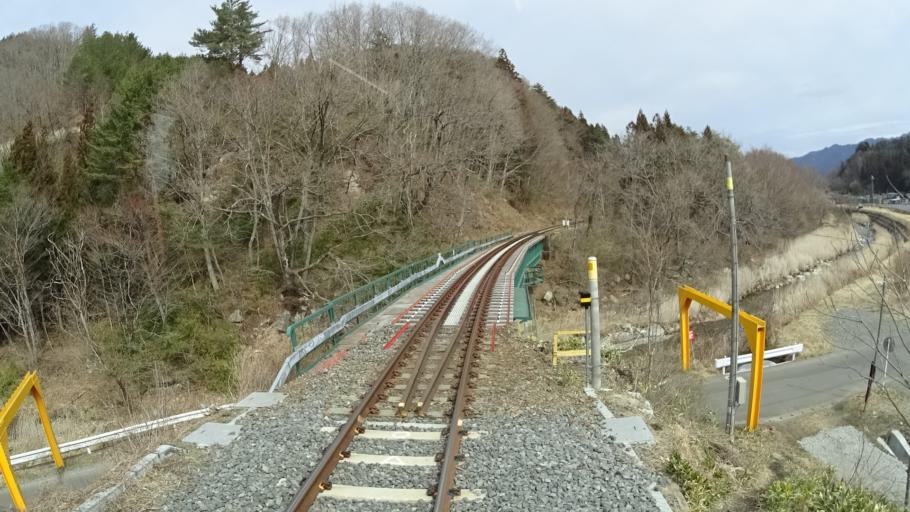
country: JP
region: Iwate
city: Yamada
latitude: 39.5124
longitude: 141.9139
